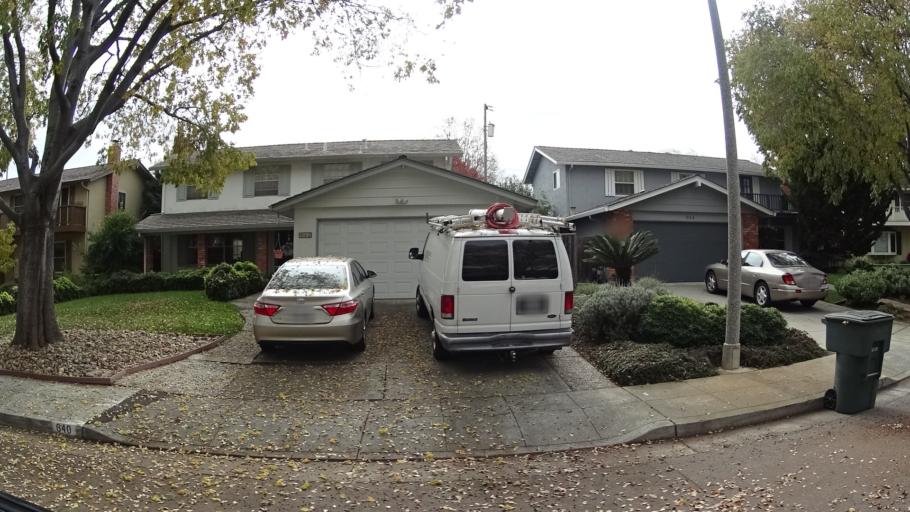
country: US
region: California
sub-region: Santa Clara County
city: Sunnyvale
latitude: 37.3614
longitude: -122.0386
